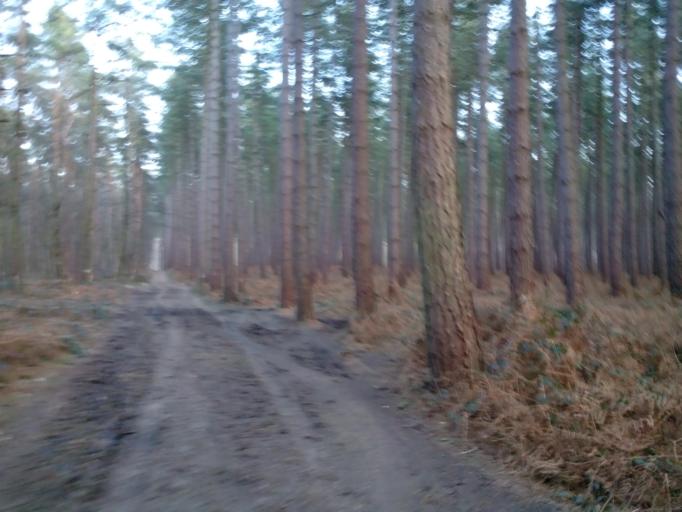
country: BE
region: Flanders
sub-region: Provincie Vlaams-Brabant
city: Oud-Heverlee
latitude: 50.8089
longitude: 4.6846
